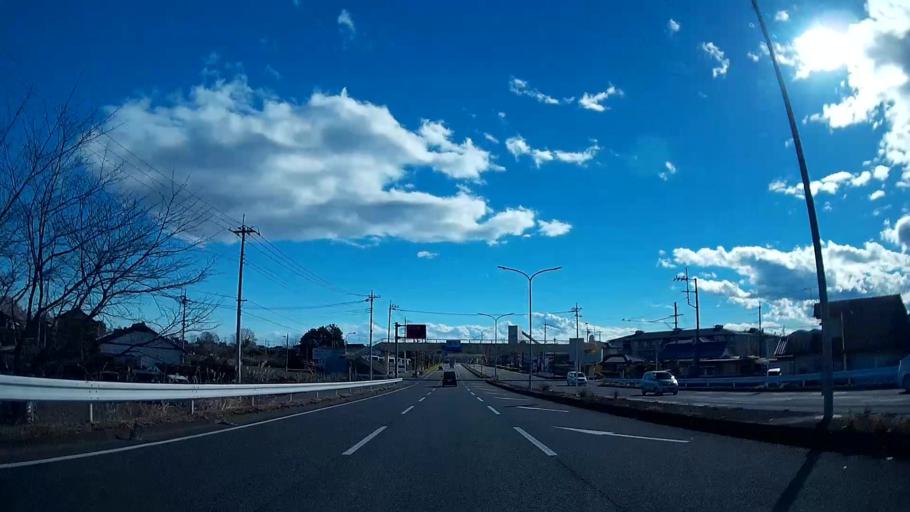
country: JP
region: Saitama
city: Yorii
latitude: 36.1246
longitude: 139.2039
